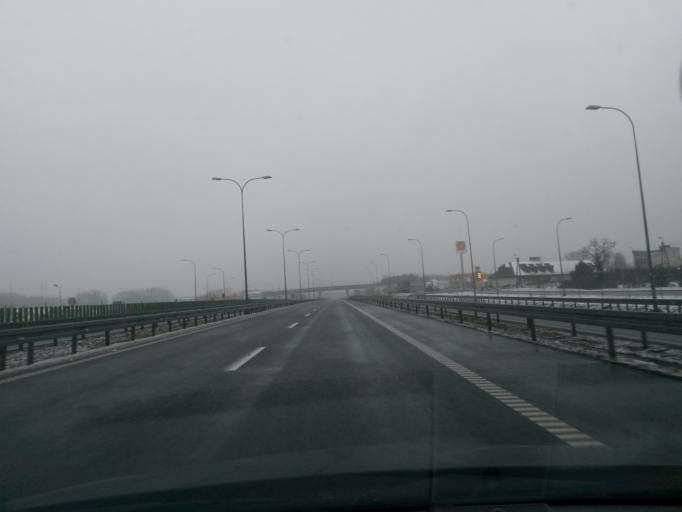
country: PL
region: Kujawsko-Pomorskie
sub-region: Powiat bydgoski
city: Biale Blota
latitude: 53.0862
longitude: 17.9049
